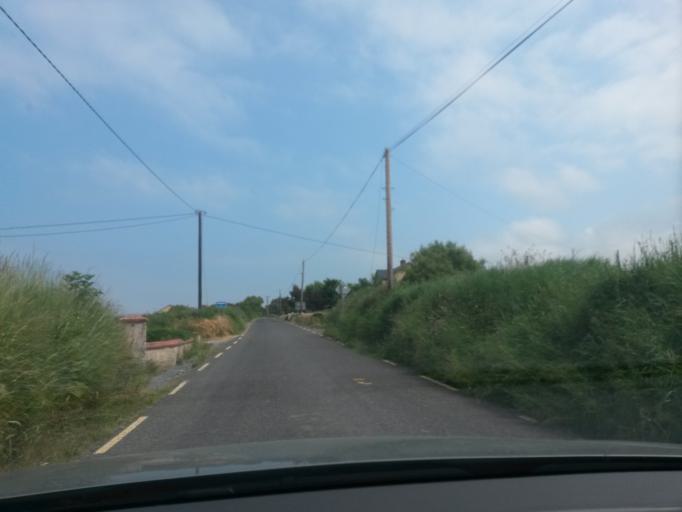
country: IE
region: Munster
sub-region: Ciarrai
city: Ballybunnion
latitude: 52.5717
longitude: -9.6233
